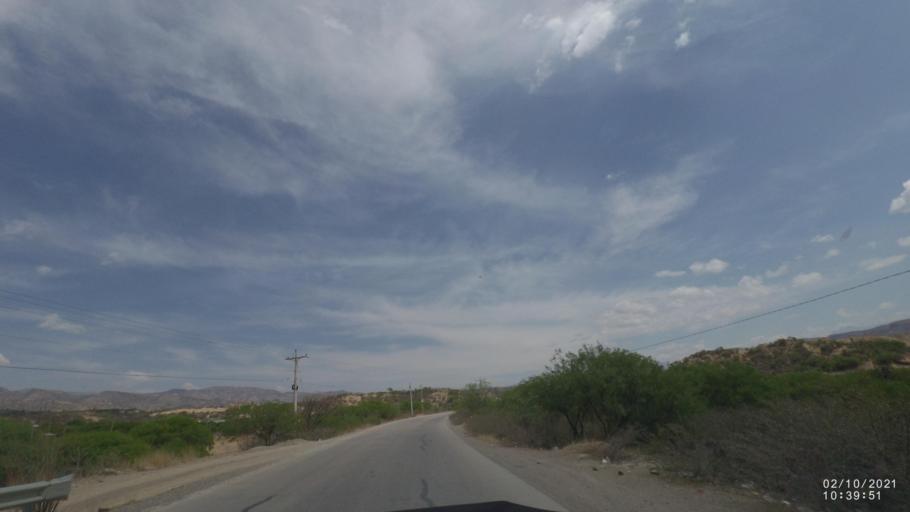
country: BO
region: Cochabamba
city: Capinota
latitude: -17.6269
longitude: -66.2793
